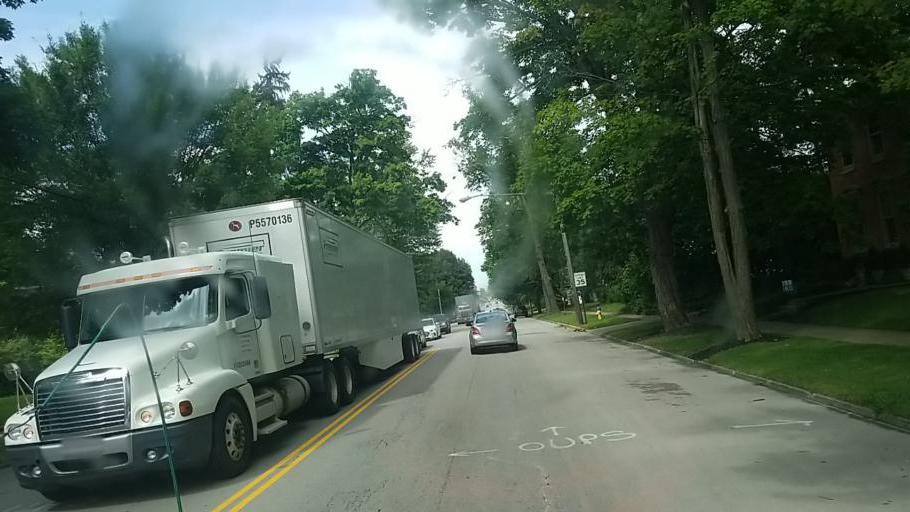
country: US
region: Ohio
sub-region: Champaign County
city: Urbana
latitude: 40.1012
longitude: -83.7532
